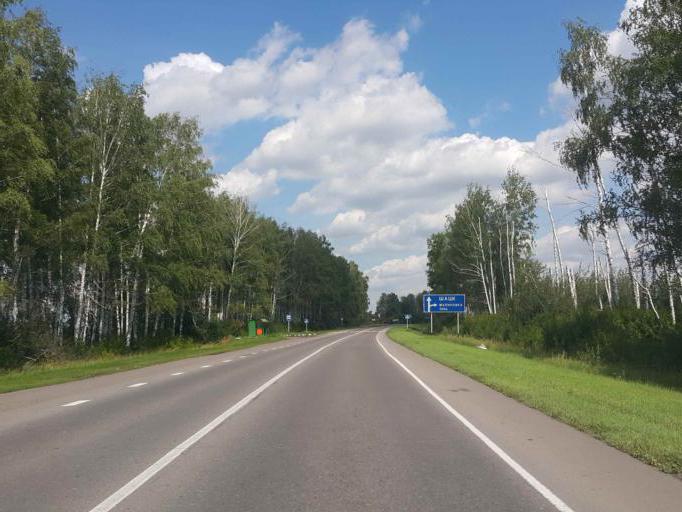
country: RU
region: Tambov
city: Goreloye
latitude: 53.0328
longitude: 41.4636
